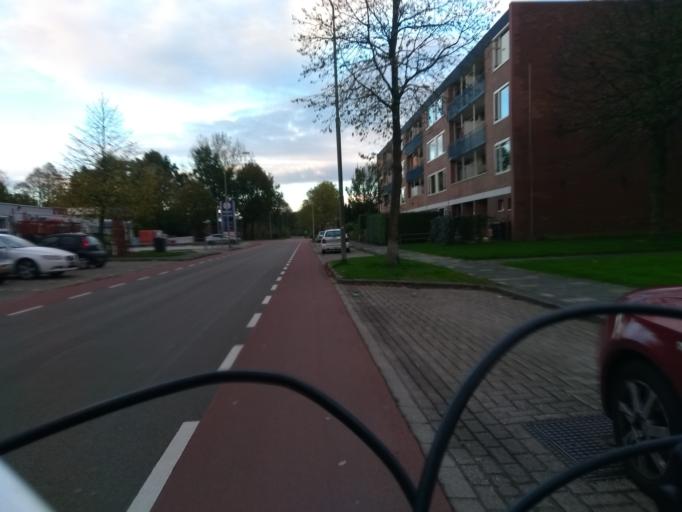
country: NL
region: Drenthe
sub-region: Gemeente Assen
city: Assen
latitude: 53.0063
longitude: 6.5581
